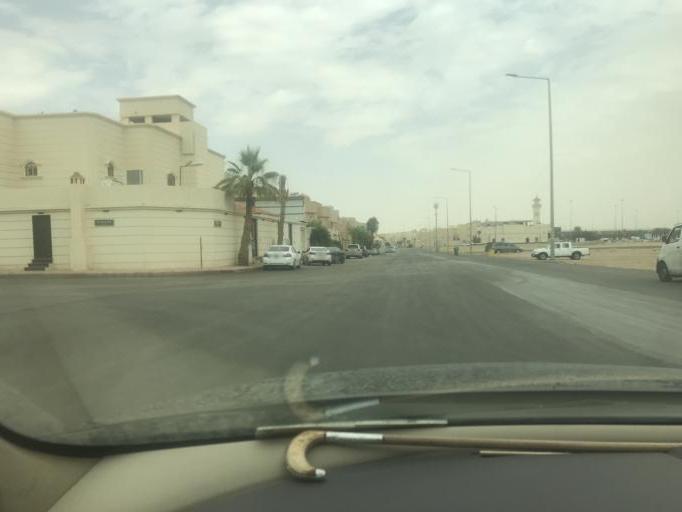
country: SA
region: Ar Riyad
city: Riyadh
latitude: 24.7903
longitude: 46.7131
